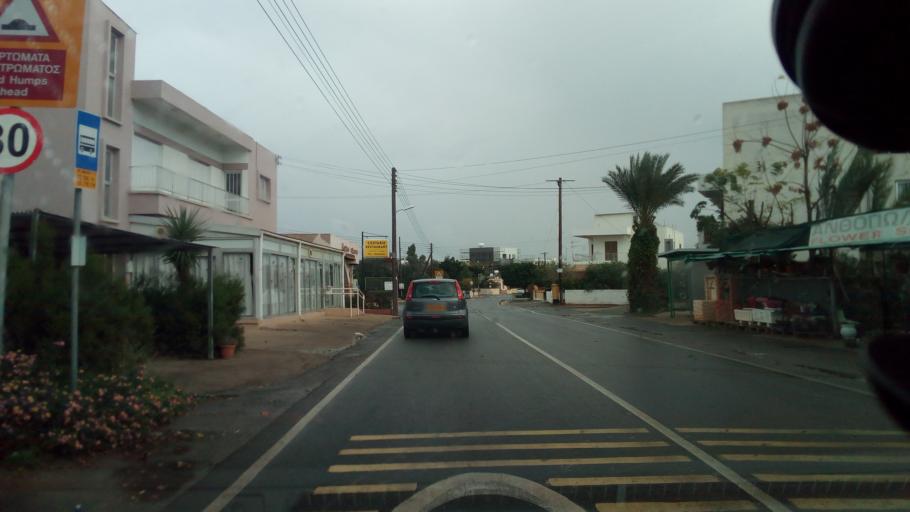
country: CY
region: Ammochostos
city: Deryneia
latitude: 35.0606
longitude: 33.9542
